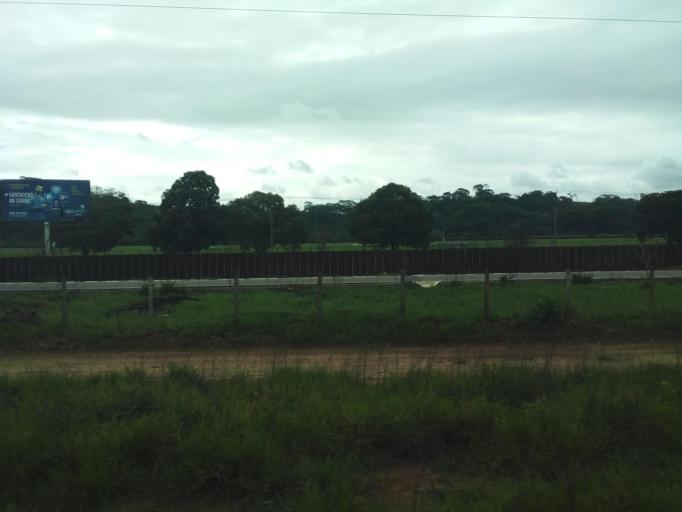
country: BR
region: Minas Gerais
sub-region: Ipatinga
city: Ipatinga
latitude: -19.4784
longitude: -42.4887
